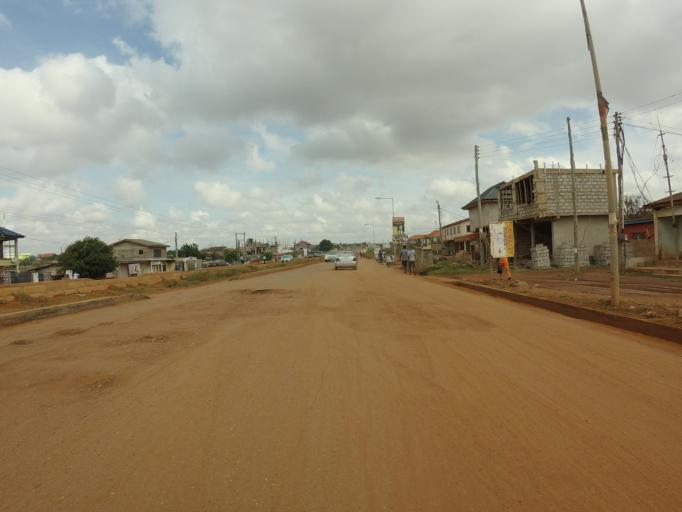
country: GH
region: Greater Accra
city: Teshi Old Town
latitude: 5.6001
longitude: -0.1197
